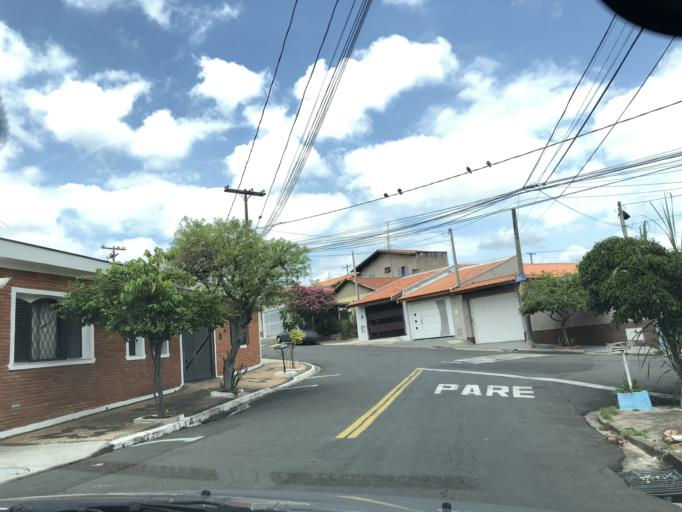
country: BR
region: Sao Paulo
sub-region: Piracicaba
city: Piracicaba
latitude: -22.7495
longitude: -47.6512
